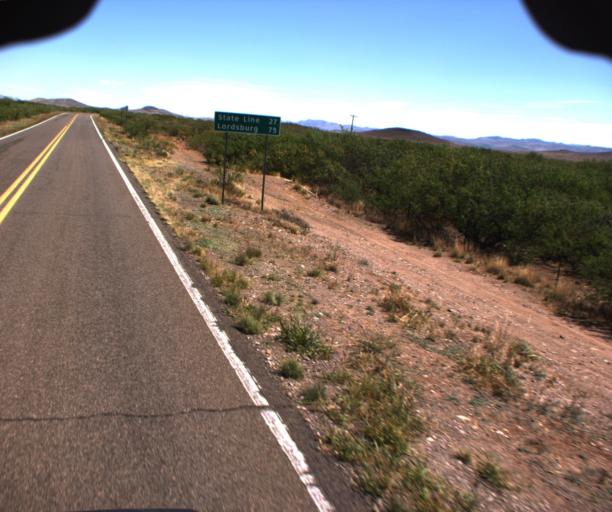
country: US
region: Arizona
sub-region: Cochise County
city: Douglas
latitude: 31.5033
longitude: -109.3191
